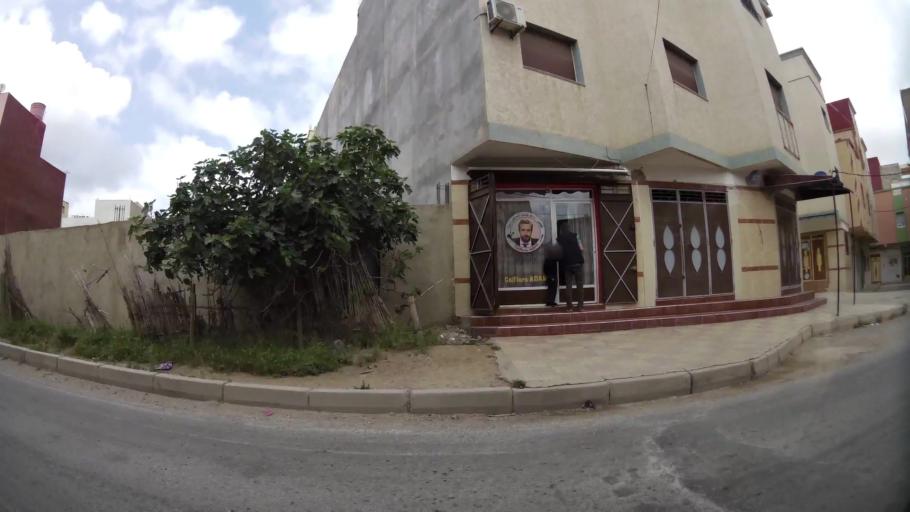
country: MA
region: Oriental
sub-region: Nador
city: Nador
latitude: 35.1618
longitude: -2.9401
